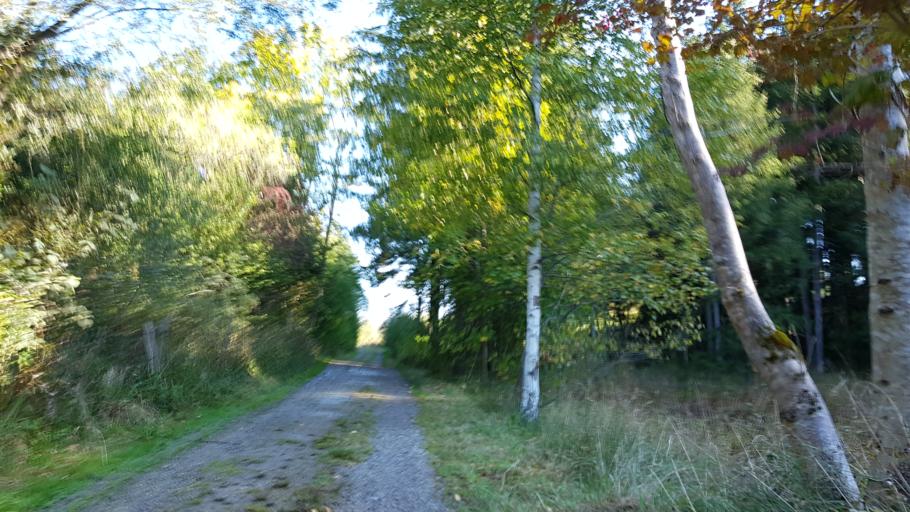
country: DE
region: Bavaria
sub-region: Swabia
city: Fuessen
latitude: 47.5770
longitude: 10.6896
